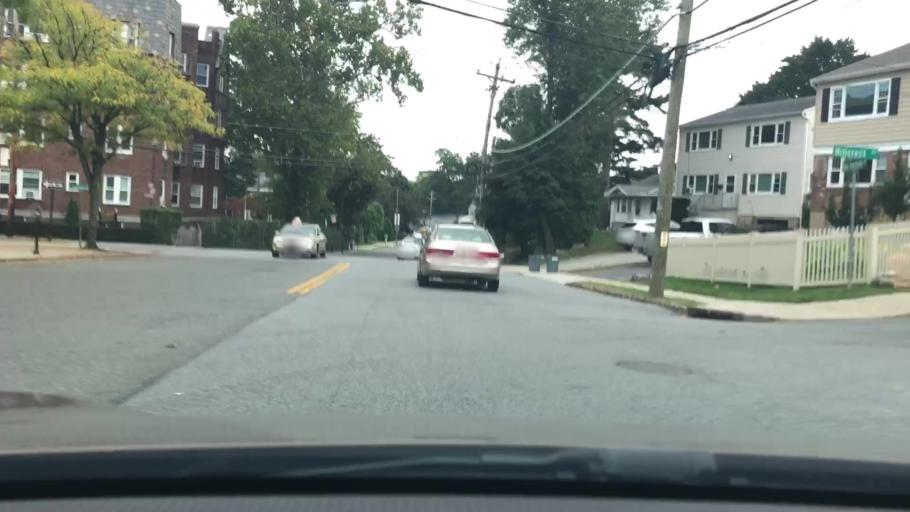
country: US
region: New York
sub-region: Westchester County
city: Pelham
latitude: 40.9283
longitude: -73.8081
